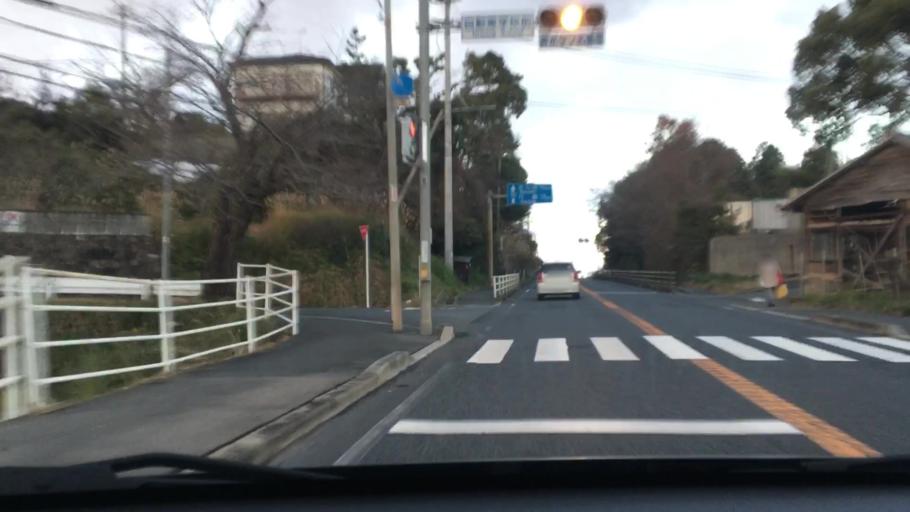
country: JP
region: Fukuoka
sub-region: Buzen-shi
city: Buzen
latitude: 33.6190
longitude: 131.0966
